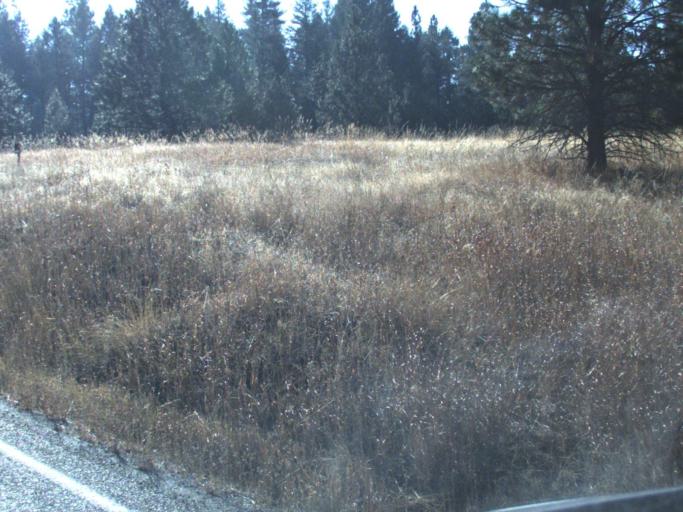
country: US
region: Washington
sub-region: Ferry County
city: Republic
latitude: 48.7310
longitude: -118.6544
